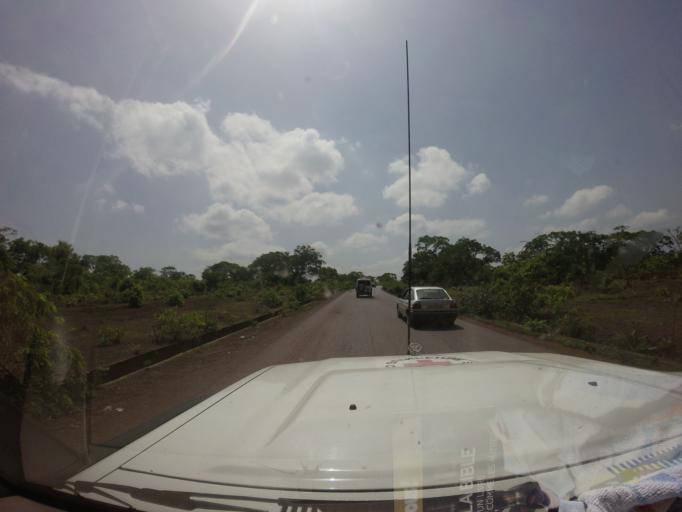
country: GN
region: Mamou
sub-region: Mamou Prefecture
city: Mamou
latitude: 10.2922
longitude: -12.3549
